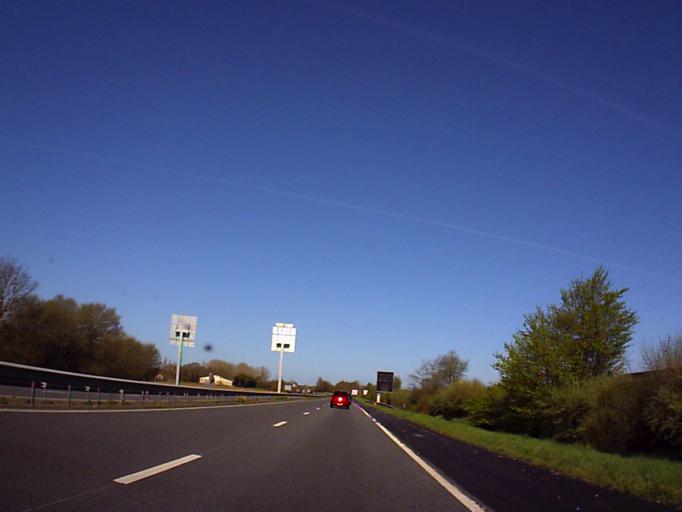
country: FR
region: Brittany
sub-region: Departement des Cotes-d'Armor
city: Plestan
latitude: 48.4139
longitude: -2.4304
